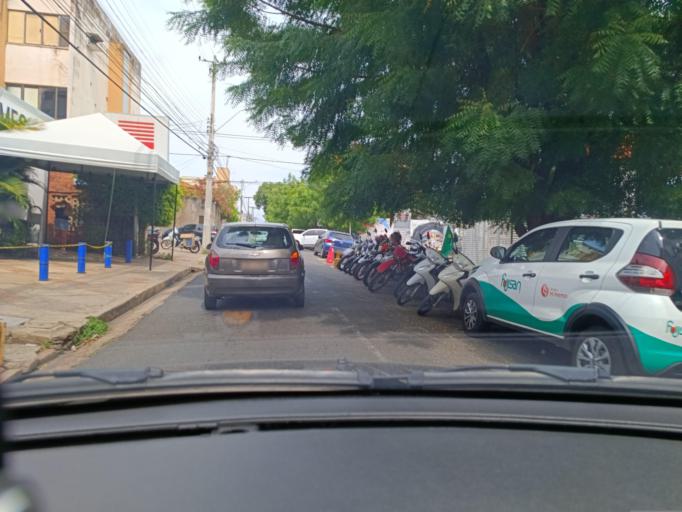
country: BR
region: Piaui
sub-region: Teresina
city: Teresina
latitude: -5.0898
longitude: -42.8078
